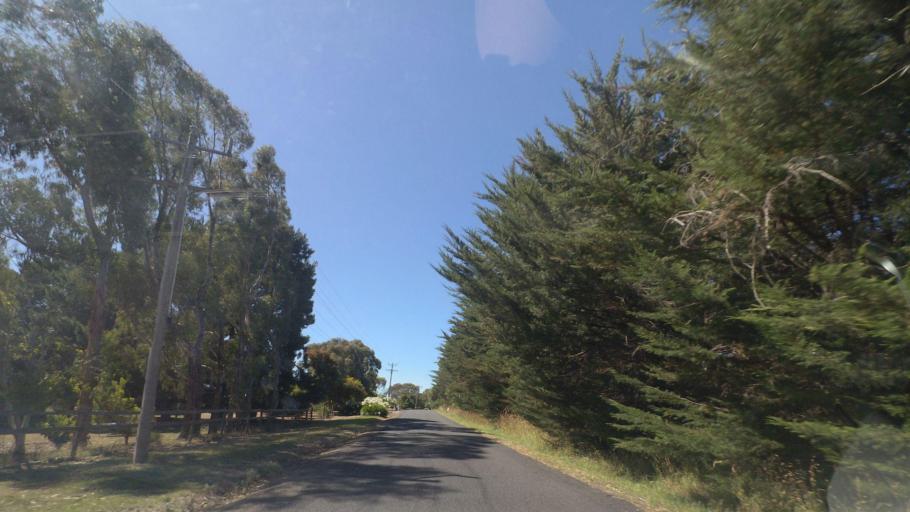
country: AU
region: Victoria
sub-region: Yarra Ranges
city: Chirnside Park
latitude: -37.7411
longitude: 145.3245
